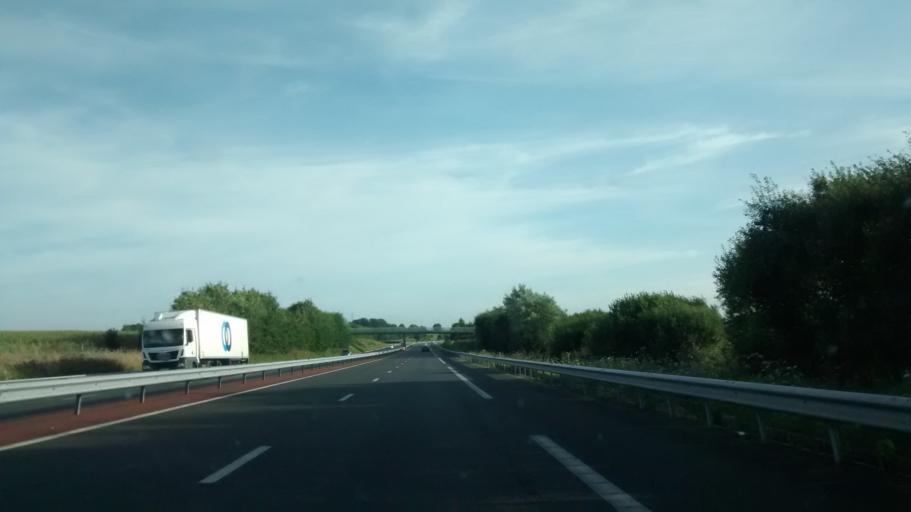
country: FR
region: Lower Normandy
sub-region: Departement de la Manche
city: Saint-Senier-sous-Avranches
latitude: 48.7575
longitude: -1.2787
